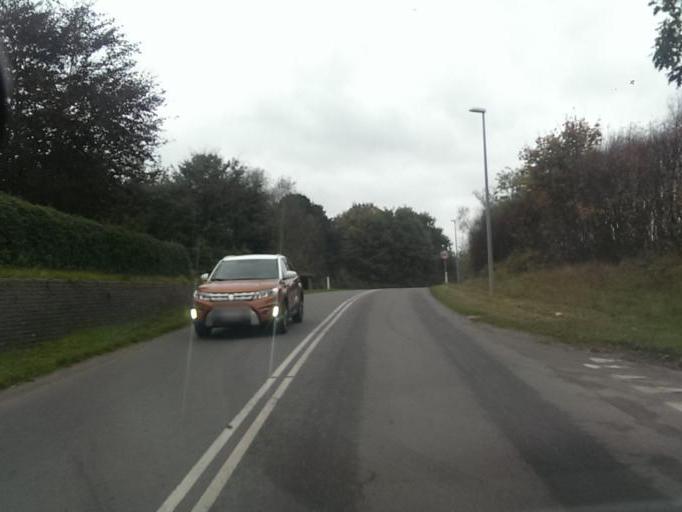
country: DK
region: South Denmark
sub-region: Esbjerg Kommune
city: Bramming
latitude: 55.4642
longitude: 8.7200
